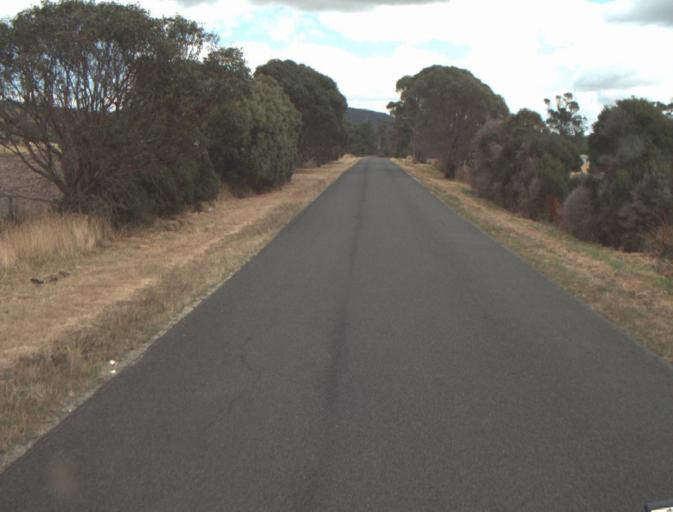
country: AU
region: Tasmania
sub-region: Launceston
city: Mayfield
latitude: -41.2074
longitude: 147.0608
